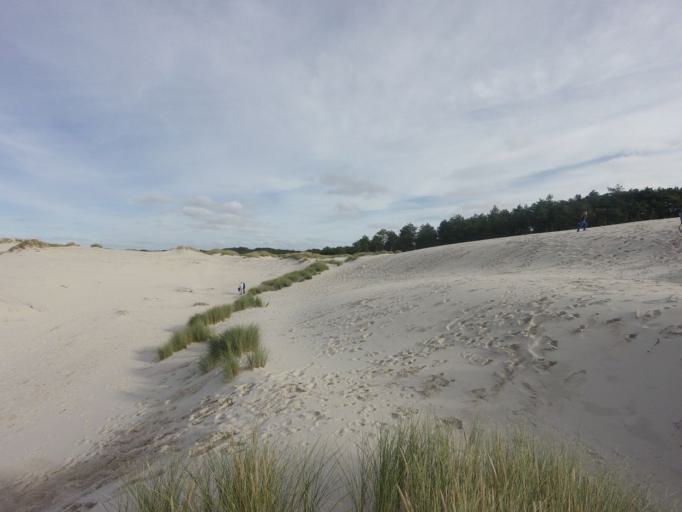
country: NL
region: North Holland
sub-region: Gemeente Bergen
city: Egmond aan Zee
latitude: 52.7122
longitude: 4.6498
